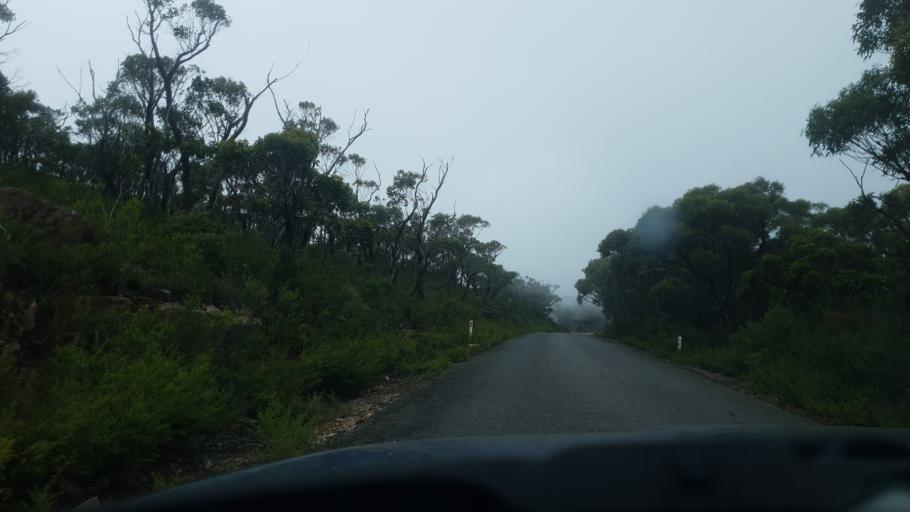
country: AU
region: Victoria
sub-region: Northern Grampians
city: Stawell
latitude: -37.2760
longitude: 142.5845
